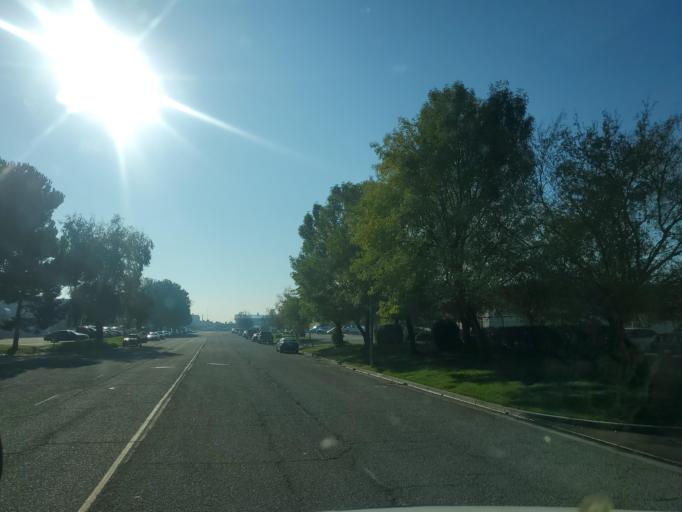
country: US
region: California
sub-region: San Joaquin County
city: French Camp
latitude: 37.8884
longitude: -121.2478
